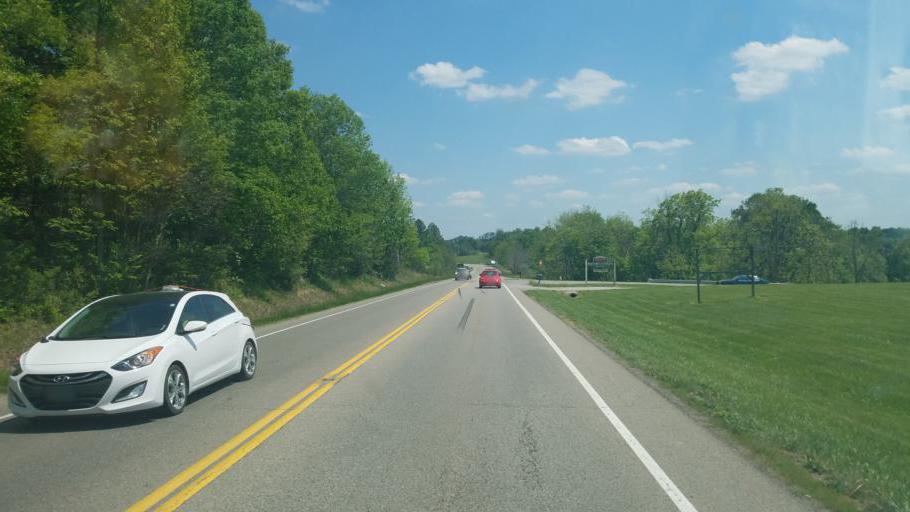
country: US
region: Ohio
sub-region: Muskingum County
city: North Zanesville
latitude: 39.9951
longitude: -82.0699
